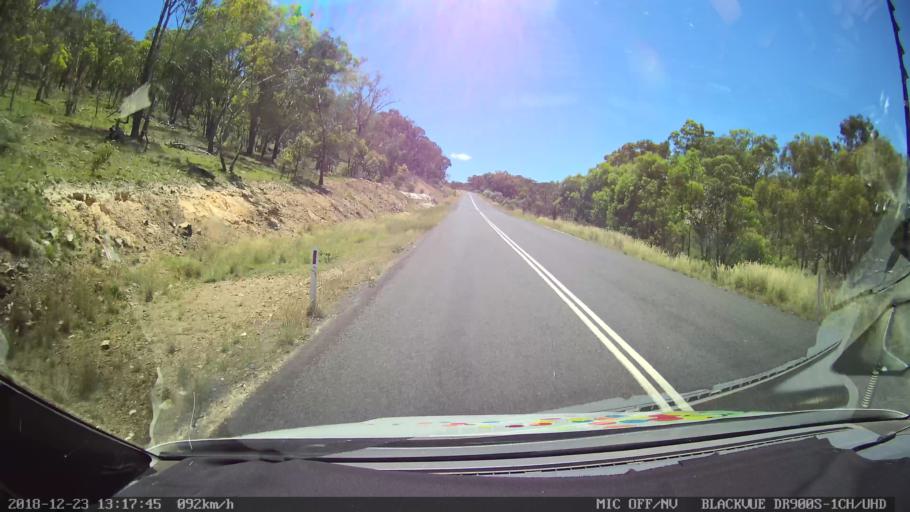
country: AU
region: New South Wales
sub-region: Armidale Dumaresq
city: Armidale
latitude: -30.4901
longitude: 151.4833
